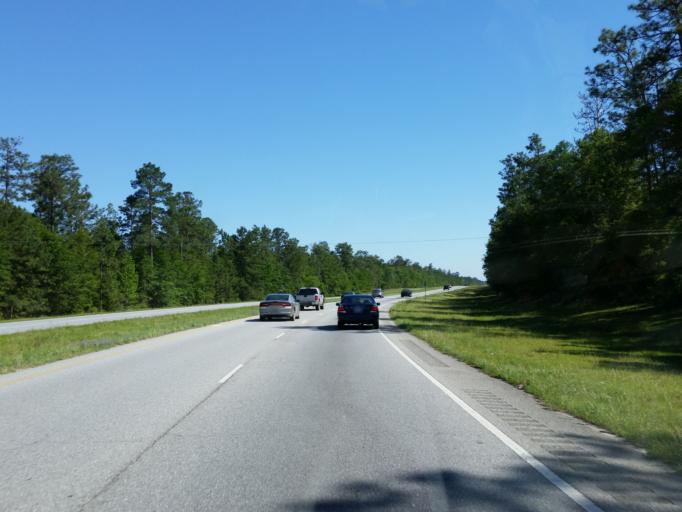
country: US
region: Georgia
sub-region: Lowndes County
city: Valdosta
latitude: 30.8718
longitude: -83.2332
